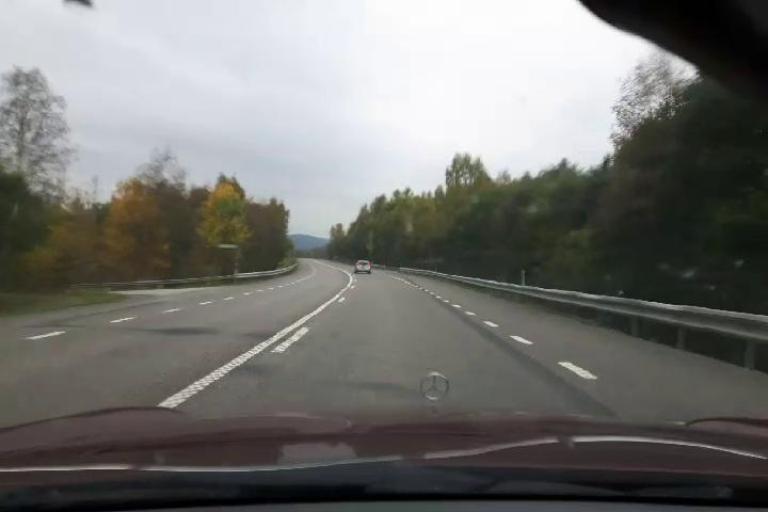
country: SE
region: Vaesternorrland
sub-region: Kramfors Kommun
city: Nordingra
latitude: 63.0206
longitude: 18.2959
